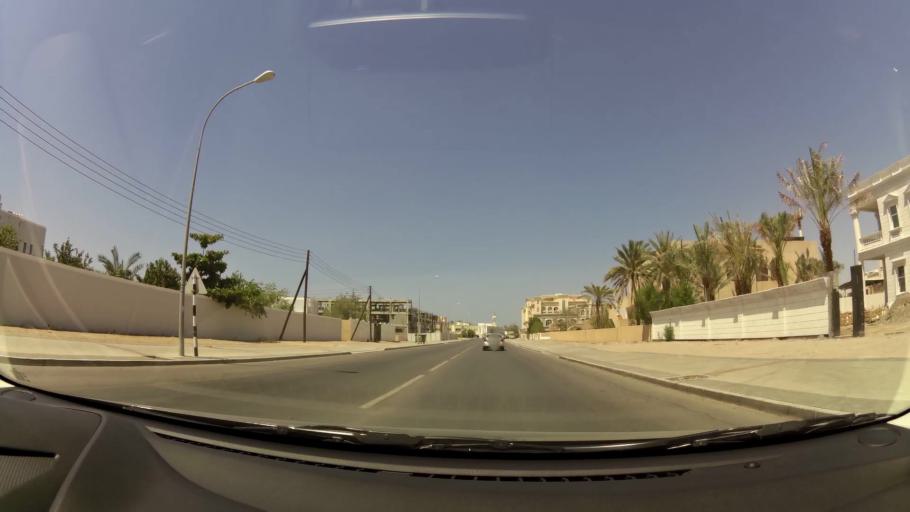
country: OM
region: Muhafazat Masqat
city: As Sib al Jadidah
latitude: 23.6303
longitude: 58.2255
